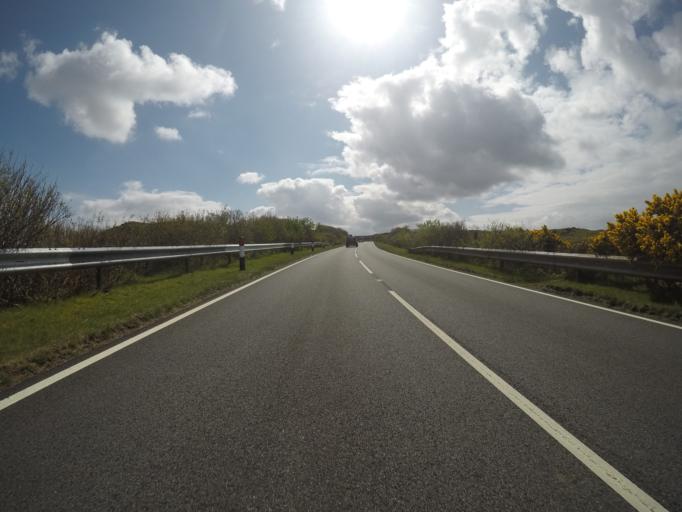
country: GB
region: Scotland
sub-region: Highland
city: Portree
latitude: 57.5196
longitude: -6.3410
